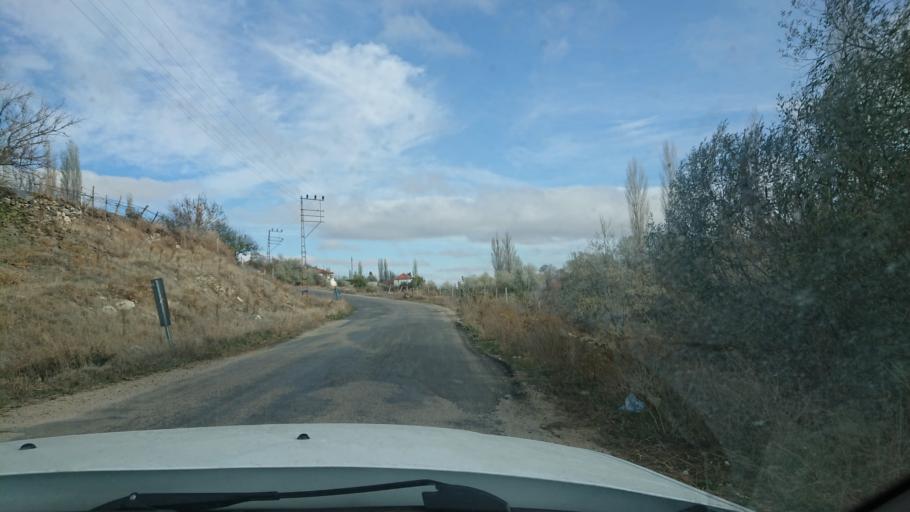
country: TR
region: Aksaray
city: Ortakoy
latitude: 38.8054
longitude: 33.9822
